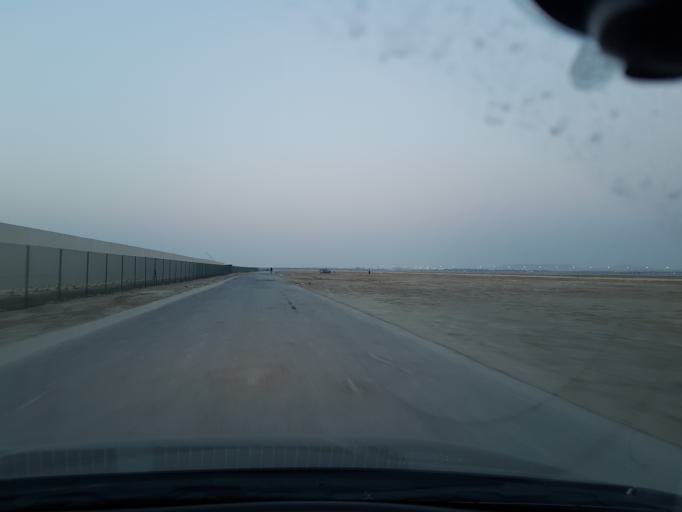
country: BH
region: Central Governorate
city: Dar Kulayb
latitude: 25.9977
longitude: 50.4703
